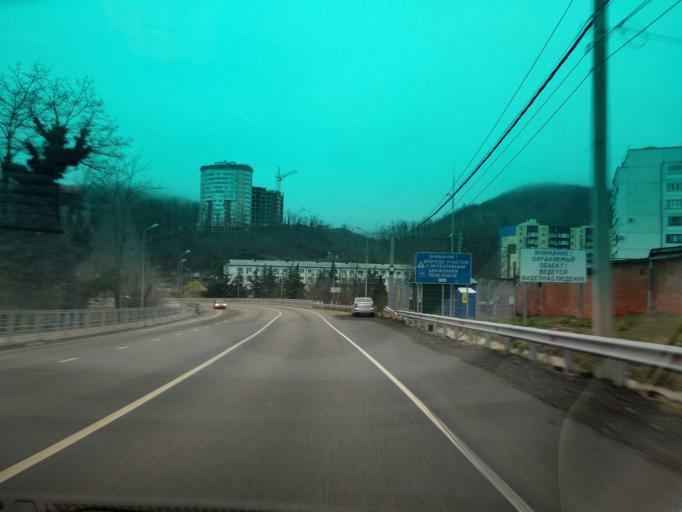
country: RU
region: Krasnodarskiy
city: Tuapse
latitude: 44.1155
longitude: 39.0686
